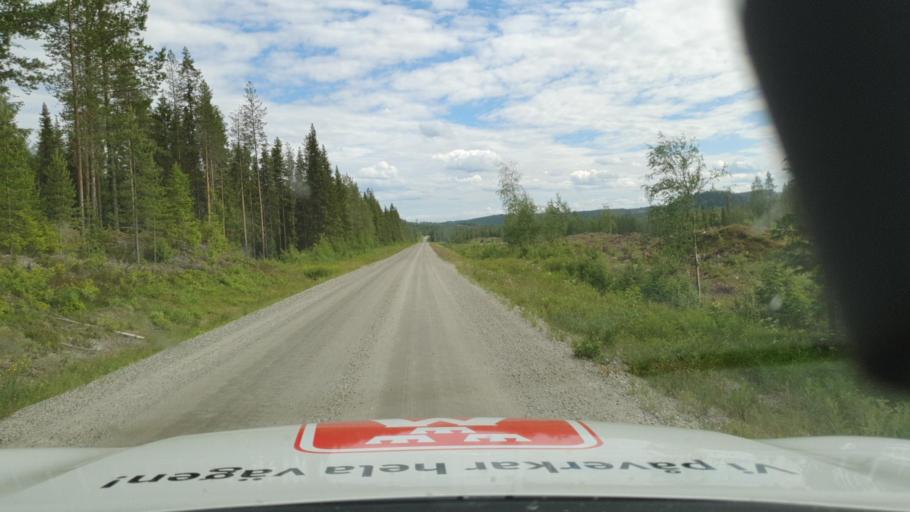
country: SE
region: Vaesterbotten
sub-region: Norsjo Kommun
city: Norsjoe
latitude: 64.8562
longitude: 19.4997
